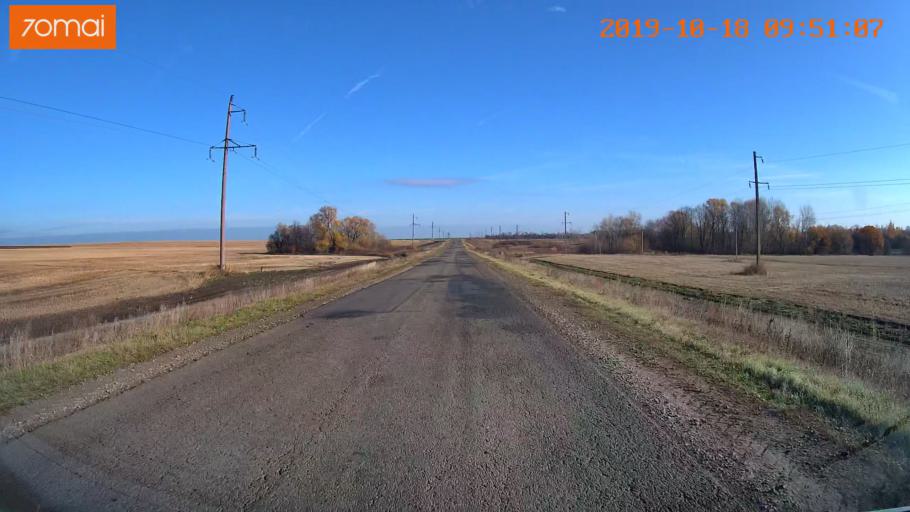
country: RU
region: Tula
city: Kazachka
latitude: 53.3366
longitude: 38.2875
